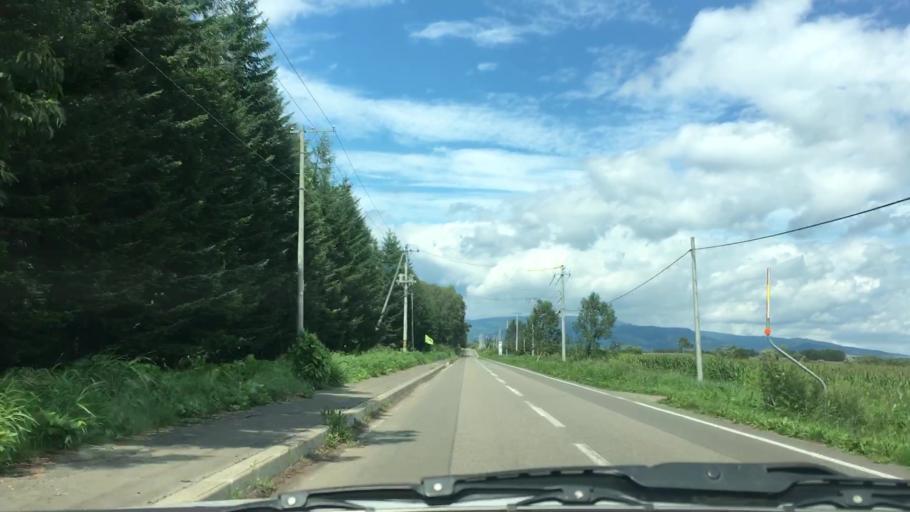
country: JP
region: Hokkaido
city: Otofuke
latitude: 43.2697
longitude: 143.3866
